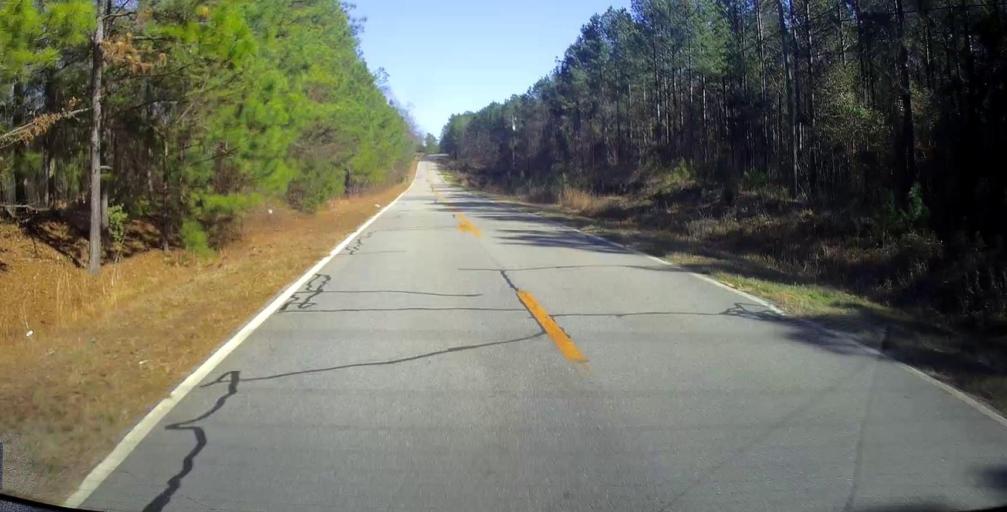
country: US
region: Georgia
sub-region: Peach County
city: Byron
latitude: 32.6112
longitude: -83.8276
